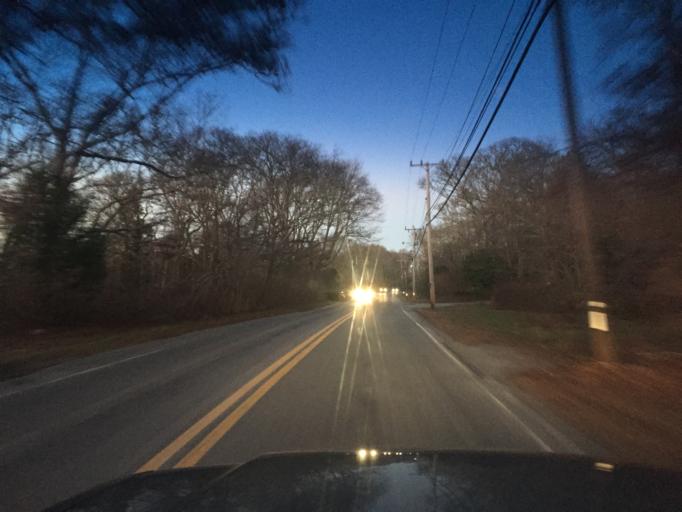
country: US
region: Massachusetts
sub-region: Barnstable County
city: West Falmouth
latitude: 41.6230
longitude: -70.6227
